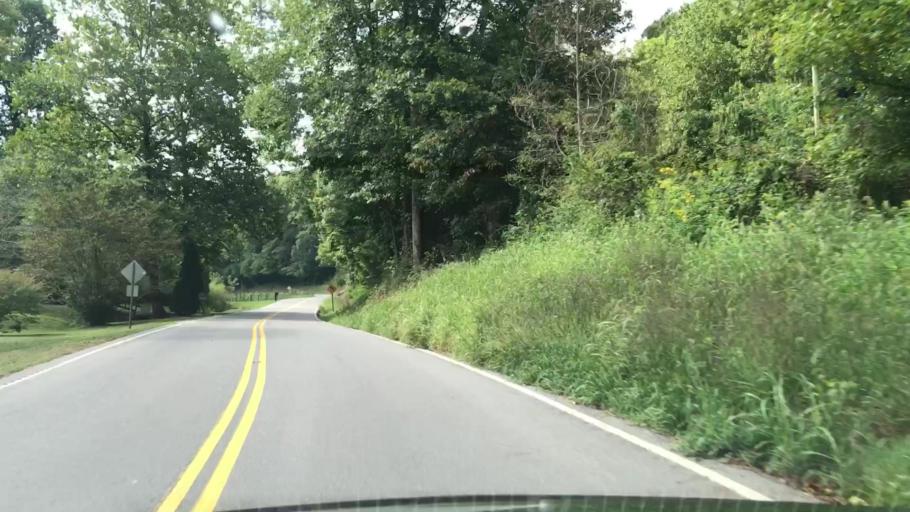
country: US
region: Tennessee
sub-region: Sumner County
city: Westmoreland
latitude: 36.4932
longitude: -86.1915
